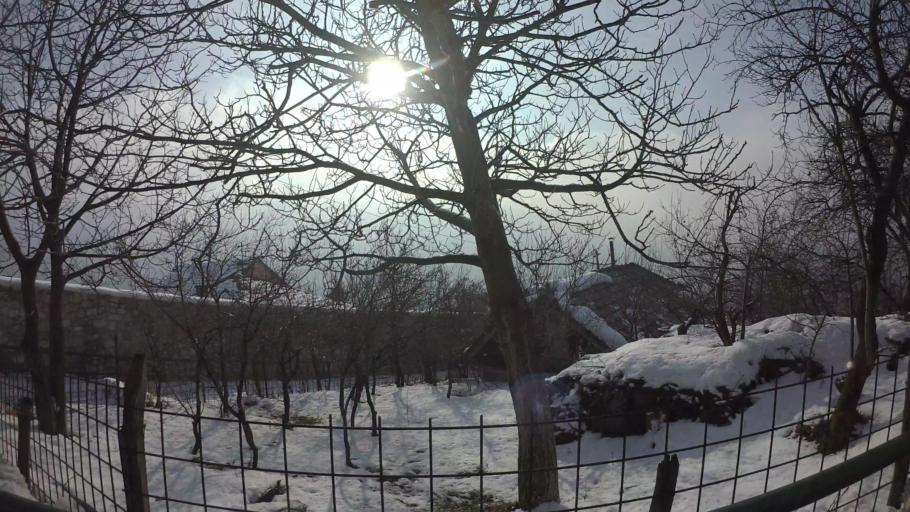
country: BA
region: Federation of Bosnia and Herzegovina
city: Kobilja Glava
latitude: 43.8657
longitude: 18.4401
